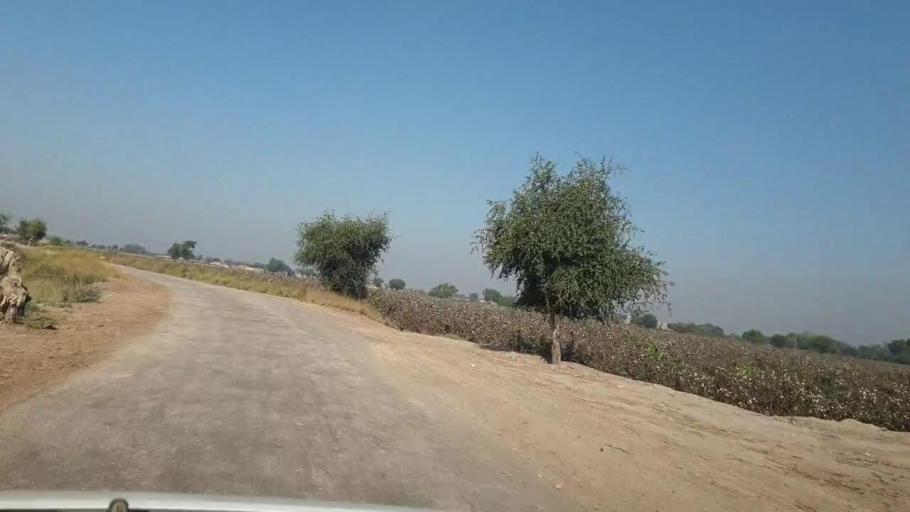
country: PK
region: Sindh
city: Bhan
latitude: 26.6049
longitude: 67.7382
